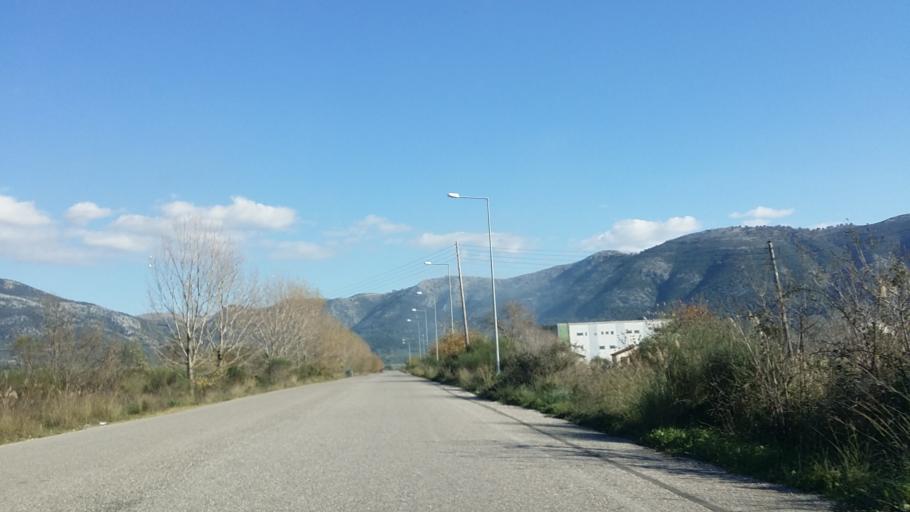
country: GR
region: West Greece
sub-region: Nomos Aitolias kai Akarnanias
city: Kandila
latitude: 38.6767
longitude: 20.9654
